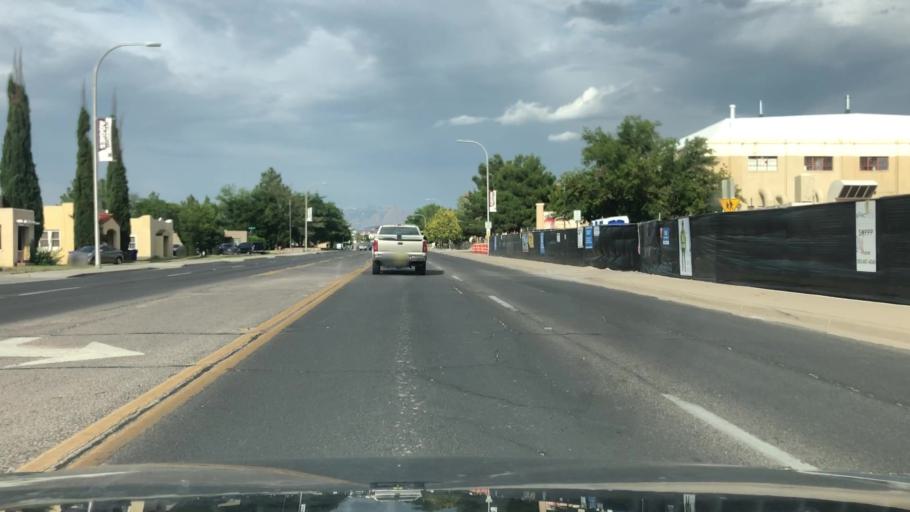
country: US
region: New Mexico
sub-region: Dona Ana County
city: University Park
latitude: 32.2848
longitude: -106.7523
